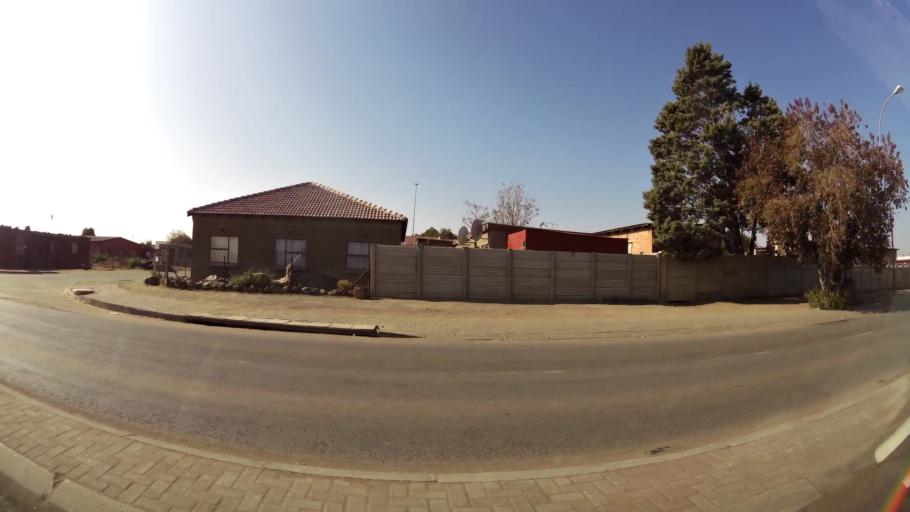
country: ZA
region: Orange Free State
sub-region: Mangaung Metropolitan Municipality
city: Bloemfontein
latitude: -29.1484
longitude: 26.2400
